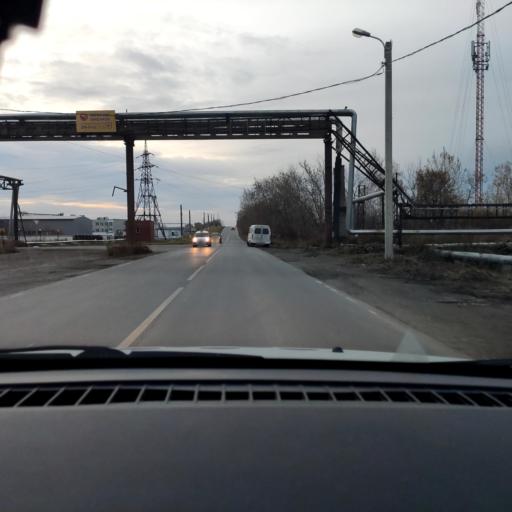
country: RU
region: Perm
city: Gamovo
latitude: 57.9133
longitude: 56.1566
